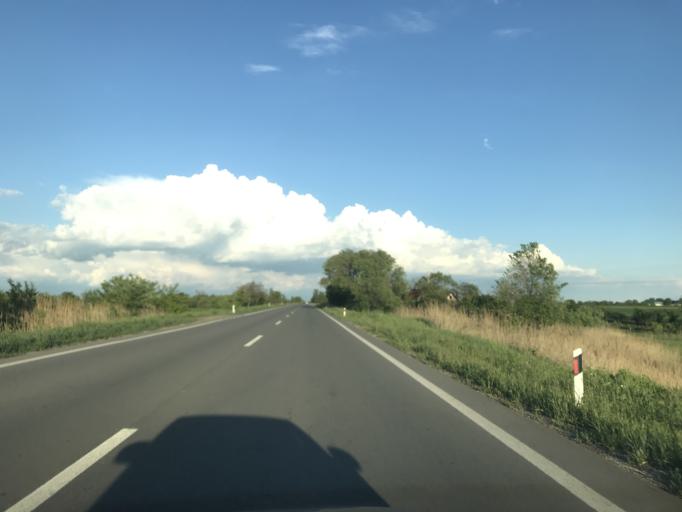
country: RS
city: Aradac
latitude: 45.3898
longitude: 20.3057
